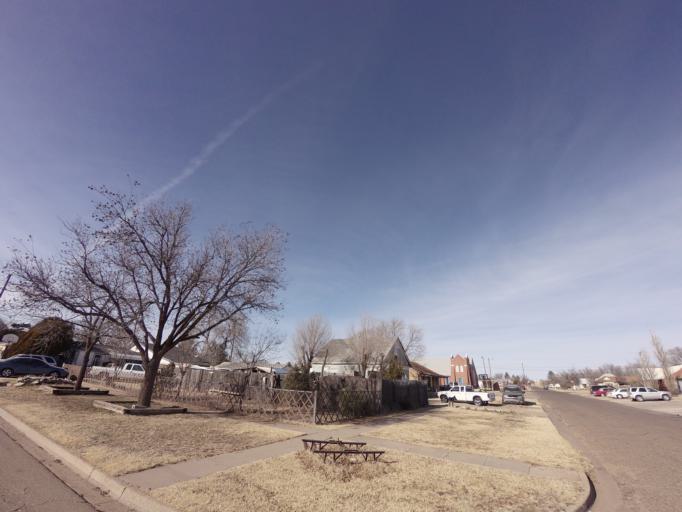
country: US
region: New Mexico
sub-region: Curry County
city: Clovis
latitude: 34.4058
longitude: -103.2155
